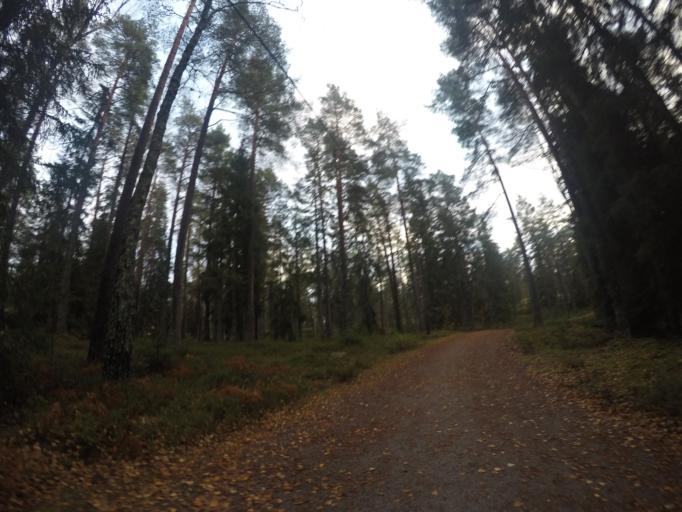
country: SE
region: Soedermanland
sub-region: Eskilstuna Kommun
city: Eskilstuna
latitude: 59.3465
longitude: 16.5259
